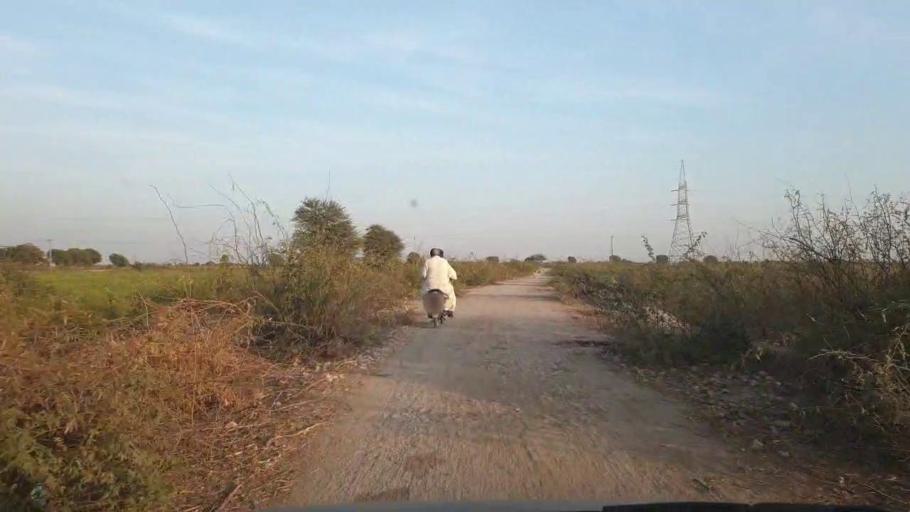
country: PK
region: Sindh
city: Chambar
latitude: 25.2838
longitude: 68.8219
